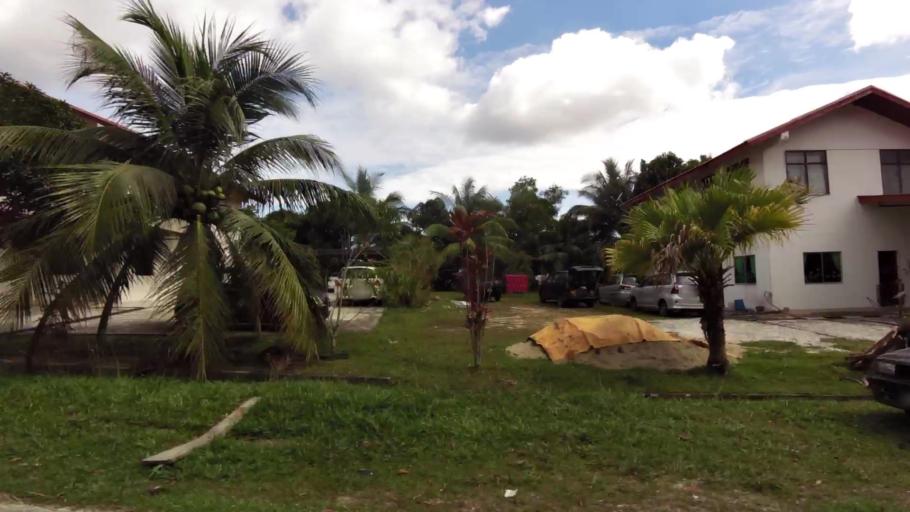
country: BN
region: Brunei and Muara
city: Bandar Seri Begawan
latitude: 4.9366
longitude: 114.9029
